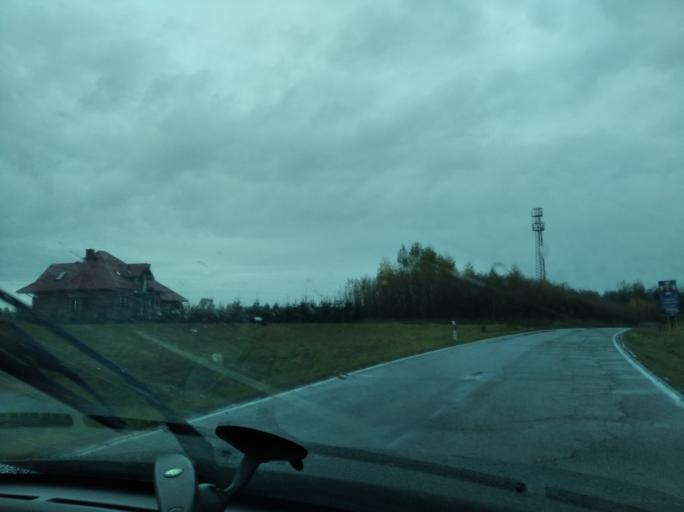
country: PL
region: Subcarpathian Voivodeship
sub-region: Powiat lancucki
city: Handzlowka
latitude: 49.9933
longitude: 22.1920
